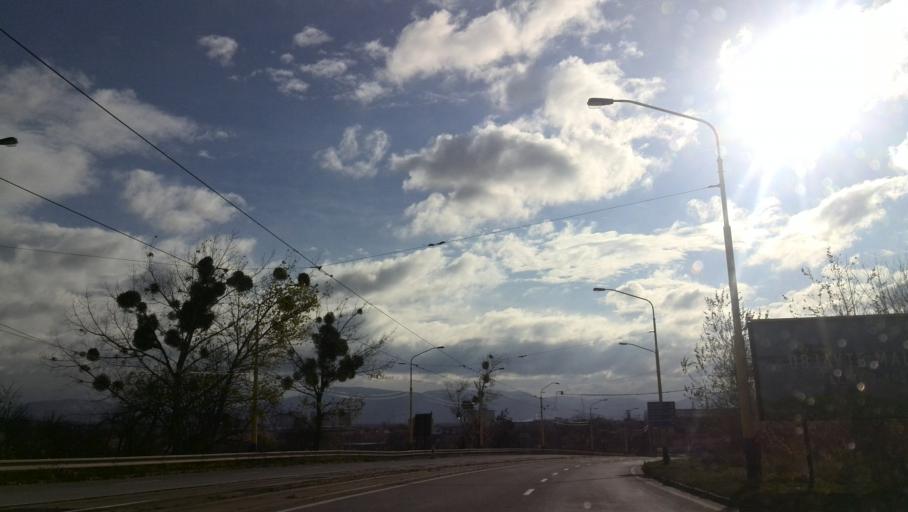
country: SK
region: Kosicky
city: Kosice
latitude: 48.6909
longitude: 21.2559
